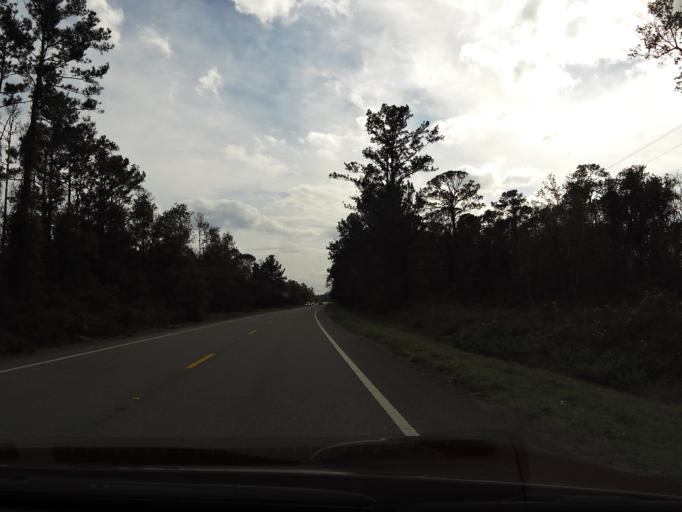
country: US
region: Florida
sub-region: Volusia County
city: De Leon Springs
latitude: 29.2059
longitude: -81.3138
